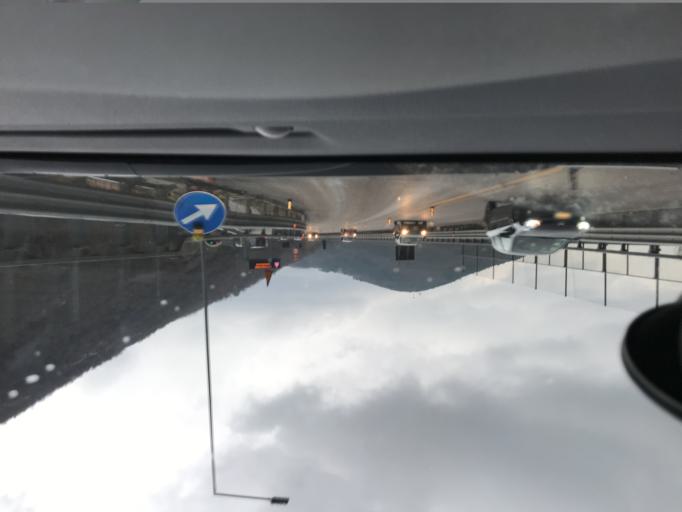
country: IT
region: The Marches
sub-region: Provincia di Ancona
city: Cerreto d'Esi
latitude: 43.3526
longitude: 12.9988
